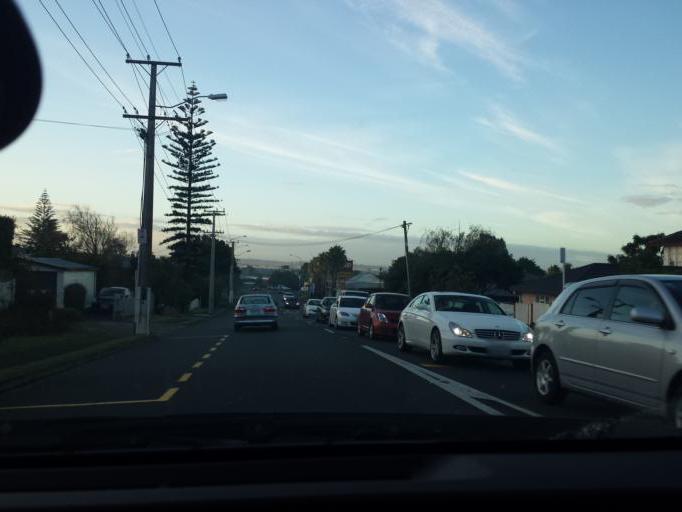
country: NZ
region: Auckland
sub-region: Auckland
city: Tamaki
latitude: -36.8948
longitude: 174.8400
